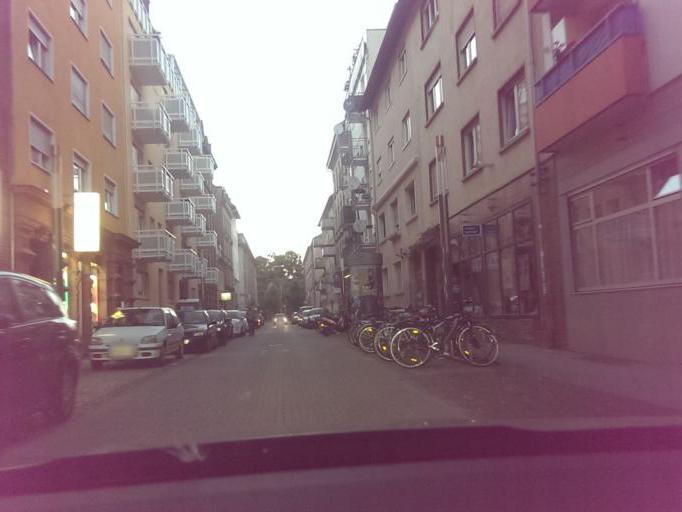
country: DE
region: Baden-Wuerttemberg
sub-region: Karlsruhe Region
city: Karlsruhe
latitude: 49.0098
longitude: 8.4080
